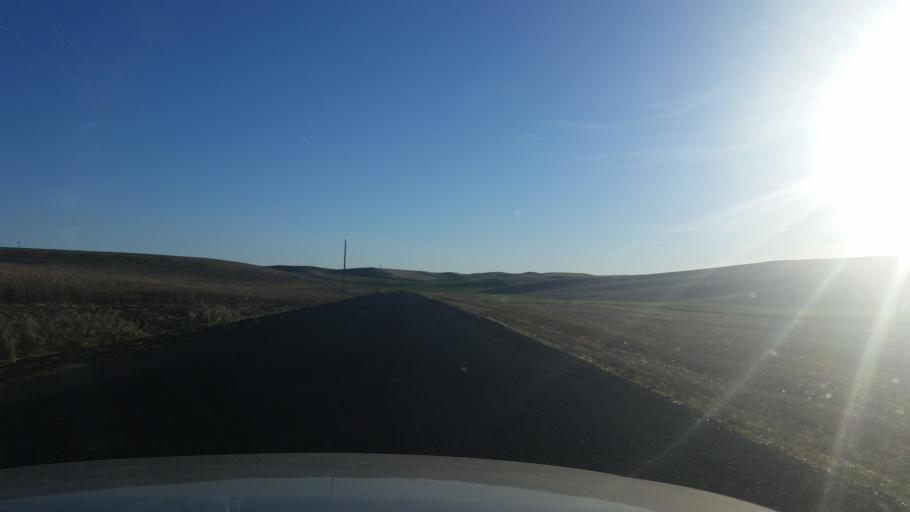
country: US
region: Washington
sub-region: Spokane County
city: Cheney
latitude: 47.3496
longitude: -117.4512
